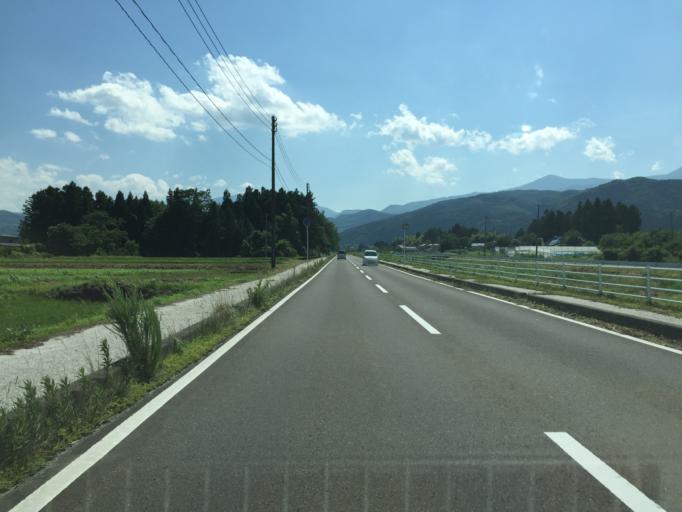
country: JP
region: Fukushima
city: Fukushima-shi
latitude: 37.7379
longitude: 140.3752
